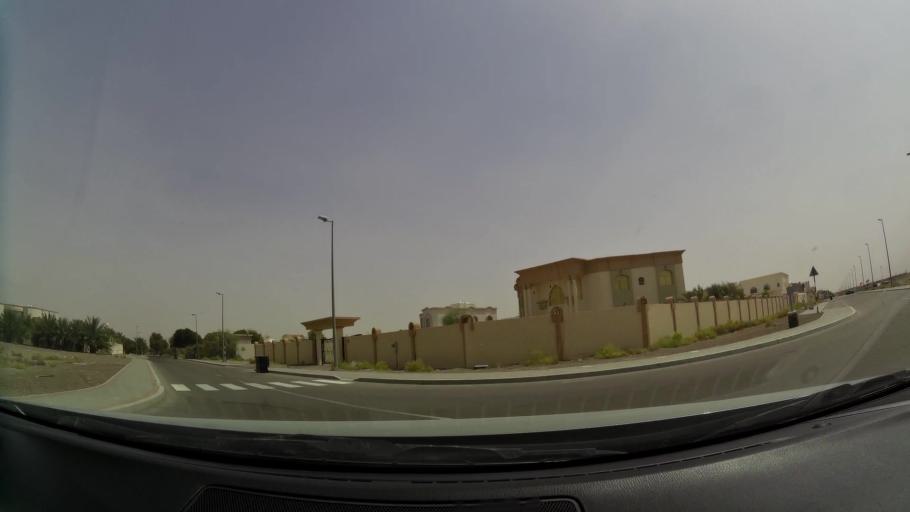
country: AE
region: Abu Dhabi
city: Al Ain
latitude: 24.1484
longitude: 55.6409
